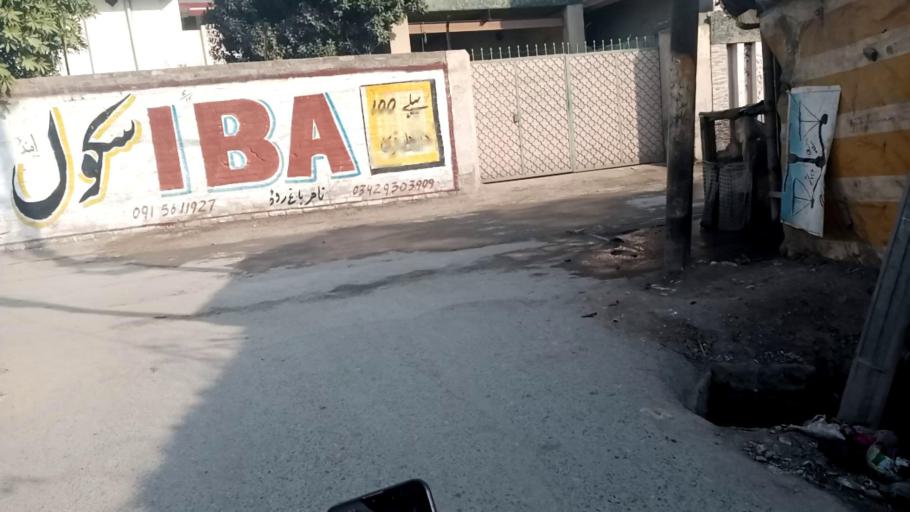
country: PK
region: Khyber Pakhtunkhwa
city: Peshawar
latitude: 34.0027
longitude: 71.4724
